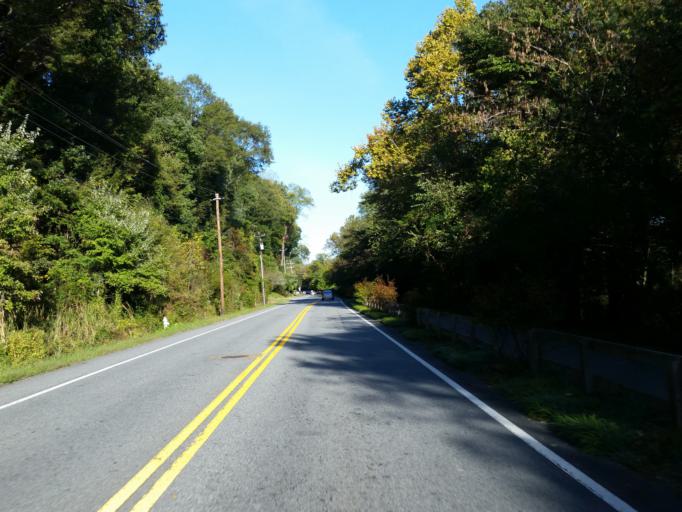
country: US
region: Georgia
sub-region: Fulton County
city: Roswell
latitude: 34.0029
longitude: -84.3602
